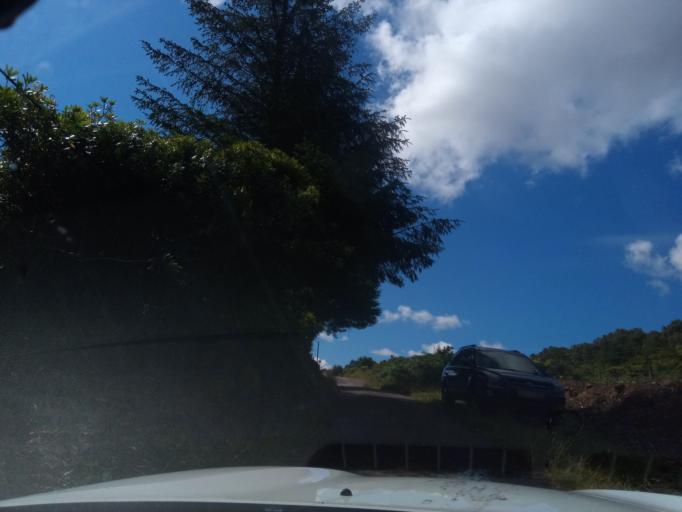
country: GB
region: Scotland
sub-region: Argyll and Bute
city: Isle Of Mull
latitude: 56.7746
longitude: -5.8245
